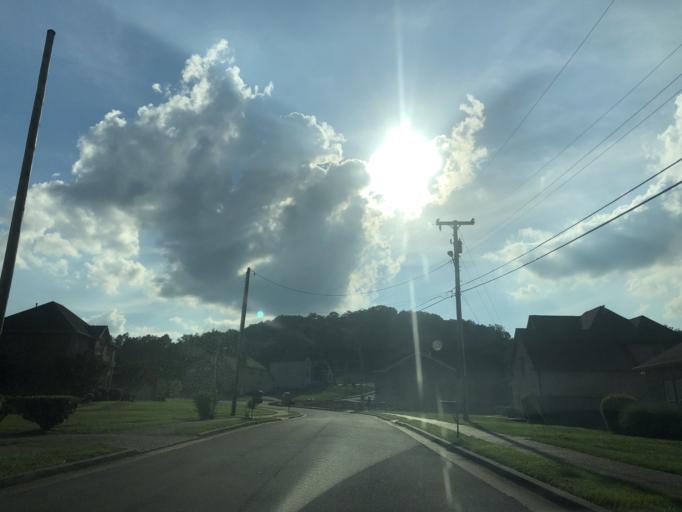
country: US
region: Tennessee
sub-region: Davidson County
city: Nashville
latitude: 36.2553
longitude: -86.8319
